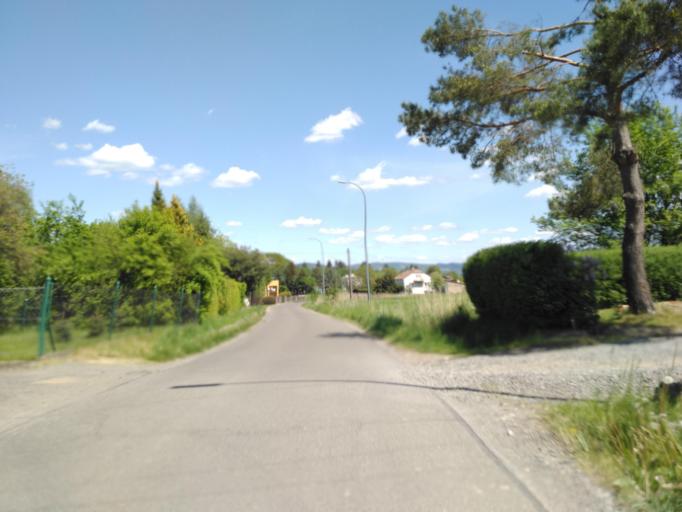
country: PL
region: Subcarpathian Voivodeship
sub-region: Powiat krosnienski
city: Jedlicze
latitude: 49.7067
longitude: 21.6923
